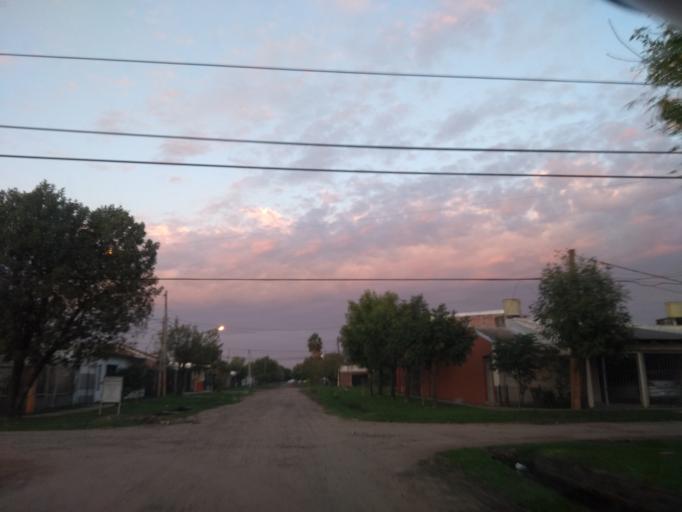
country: AR
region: Chaco
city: Resistencia
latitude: -27.4765
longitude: -58.9822
